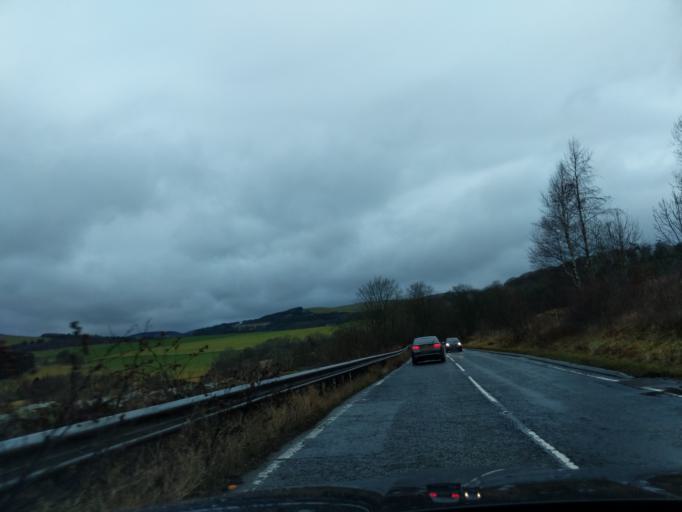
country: GB
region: Scotland
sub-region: The Scottish Borders
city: Galashiels
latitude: 55.6420
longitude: -2.8457
